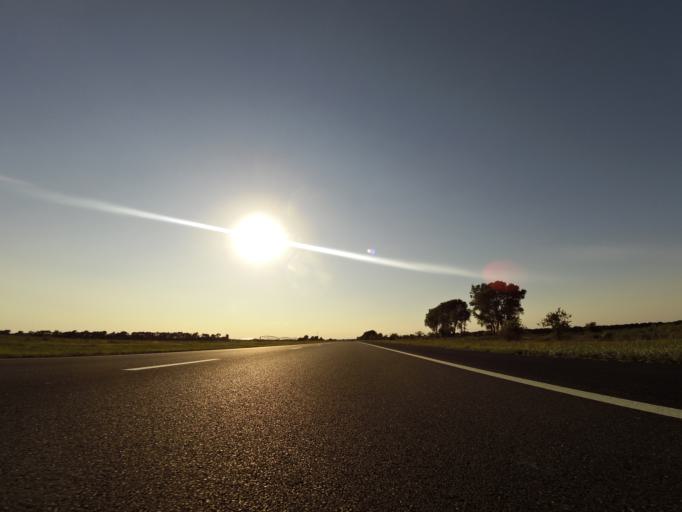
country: US
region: Kansas
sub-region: Reno County
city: Haven
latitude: 37.8878
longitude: -97.7397
